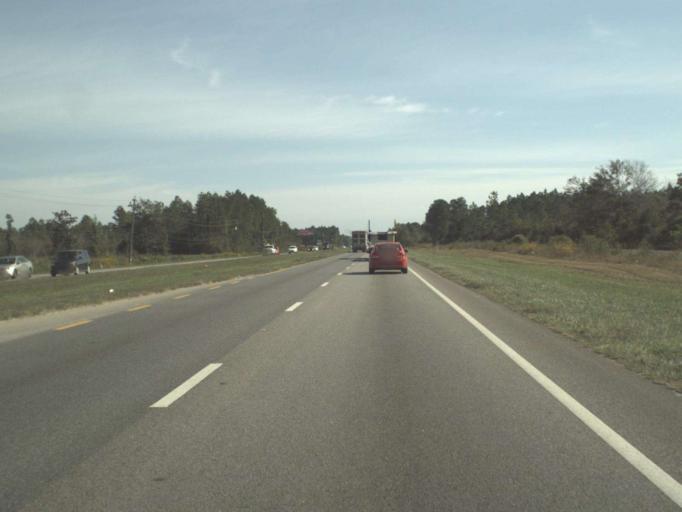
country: US
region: Florida
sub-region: Bay County
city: Hiland Park
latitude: 30.2346
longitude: -85.5770
